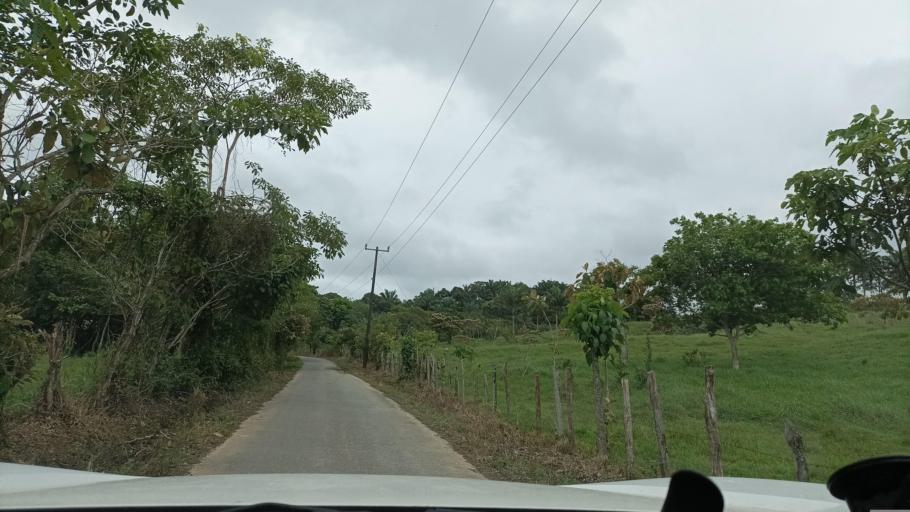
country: MX
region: Veracruz
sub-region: Moloacan
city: Cuichapa
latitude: 17.8524
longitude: -94.3548
